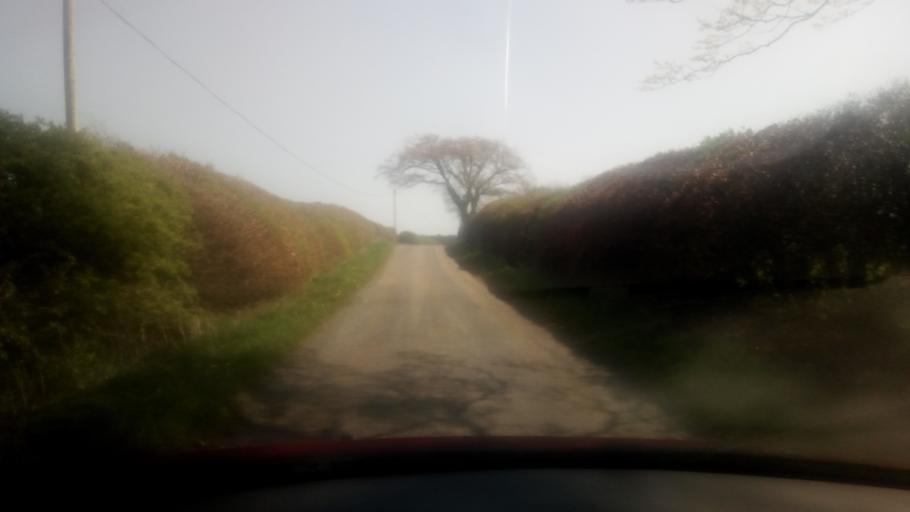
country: GB
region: Scotland
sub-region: The Scottish Borders
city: Jedburgh
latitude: 55.4703
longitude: -2.4645
